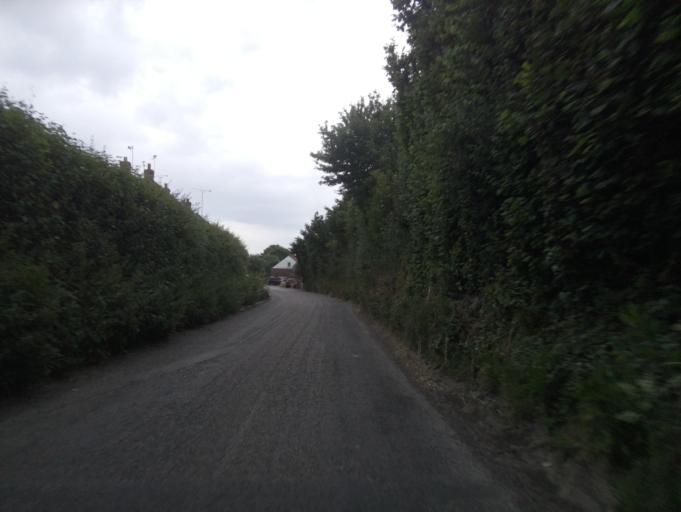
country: GB
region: England
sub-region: Somerset
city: Yeovil
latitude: 50.9166
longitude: -2.6183
